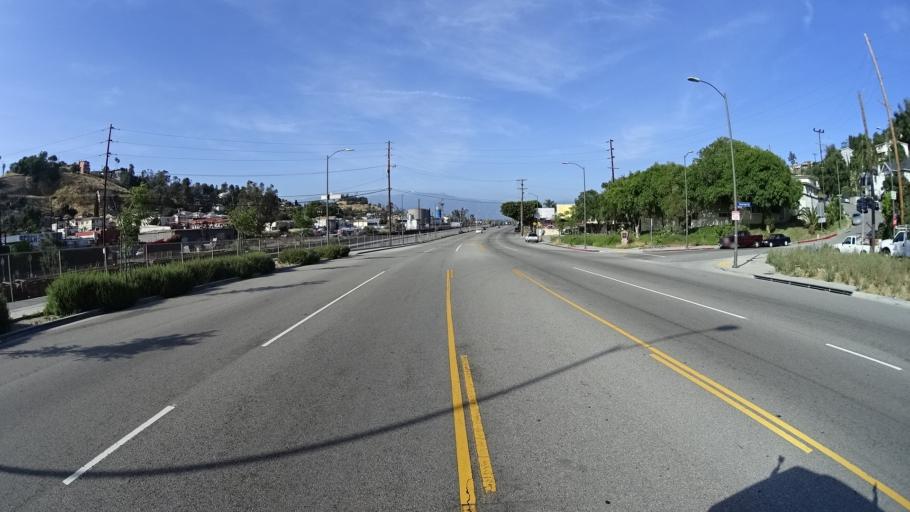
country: US
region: California
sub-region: Los Angeles County
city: Belvedere
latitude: 34.0687
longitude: -118.1759
